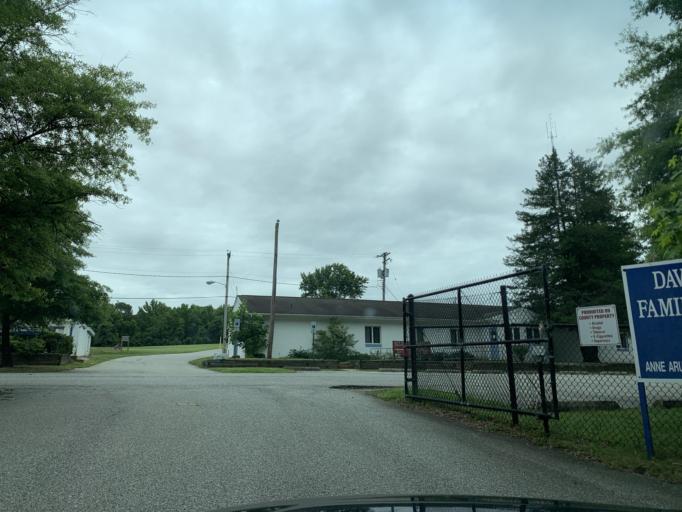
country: US
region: Maryland
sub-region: Anne Arundel County
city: Davidsonville
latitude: 38.9043
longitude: -76.6528
